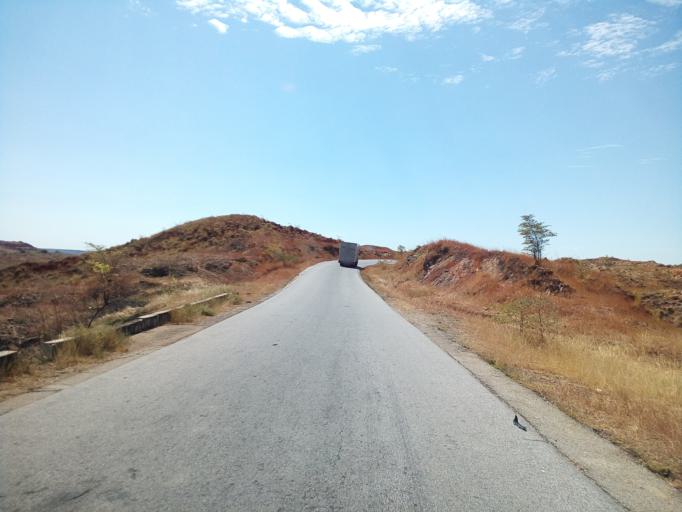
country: MG
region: Betsiboka
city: Maevatanana
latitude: -16.9457
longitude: 46.8550
